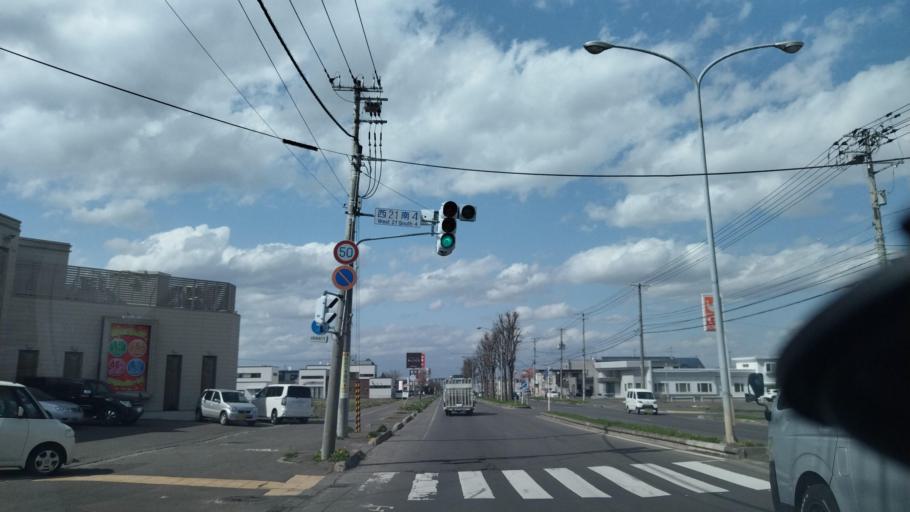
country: JP
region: Hokkaido
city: Obihiro
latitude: 42.9078
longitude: 143.1457
